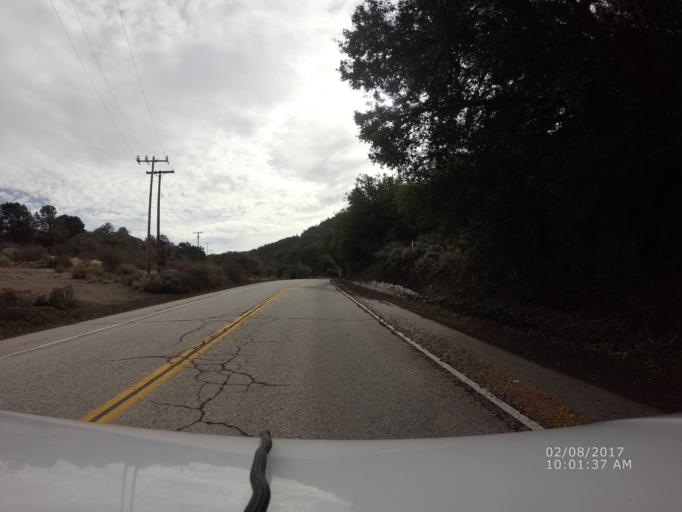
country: US
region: California
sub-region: San Bernardino County
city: Pinon Hills
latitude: 34.4010
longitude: -117.7496
